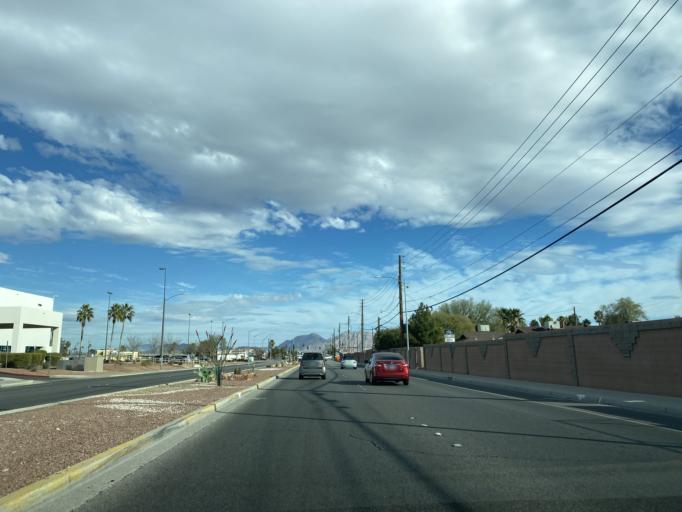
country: US
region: Nevada
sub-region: Clark County
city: Las Vegas
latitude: 36.1884
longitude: -115.1638
